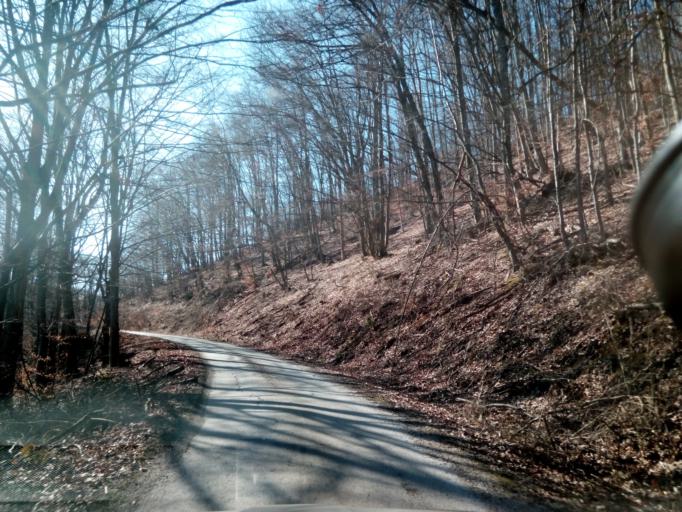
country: SK
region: Kosicky
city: Roznava
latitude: 48.5512
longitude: 20.5661
